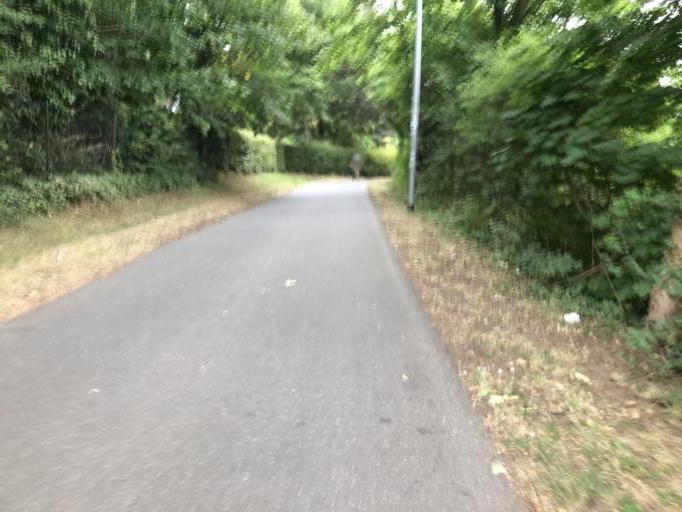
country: DE
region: Bavaria
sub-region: Regierungsbezirk Mittelfranken
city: Furth
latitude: 49.5047
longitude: 10.9761
